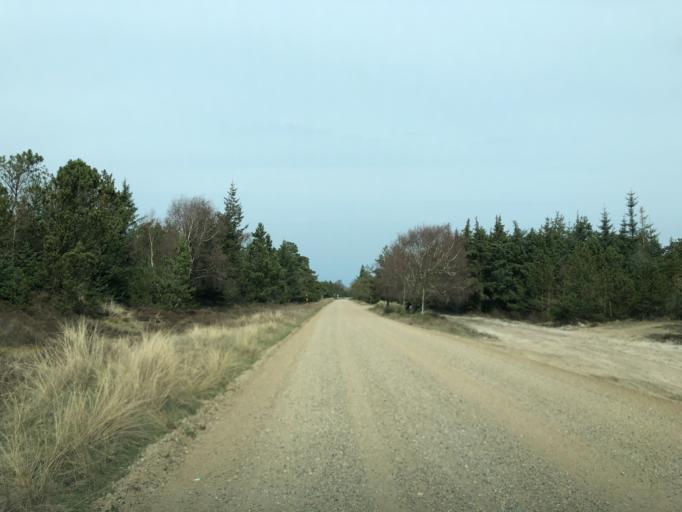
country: DK
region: South Denmark
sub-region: Varde Kommune
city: Oksbol
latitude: 55.6149
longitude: 8.1667
